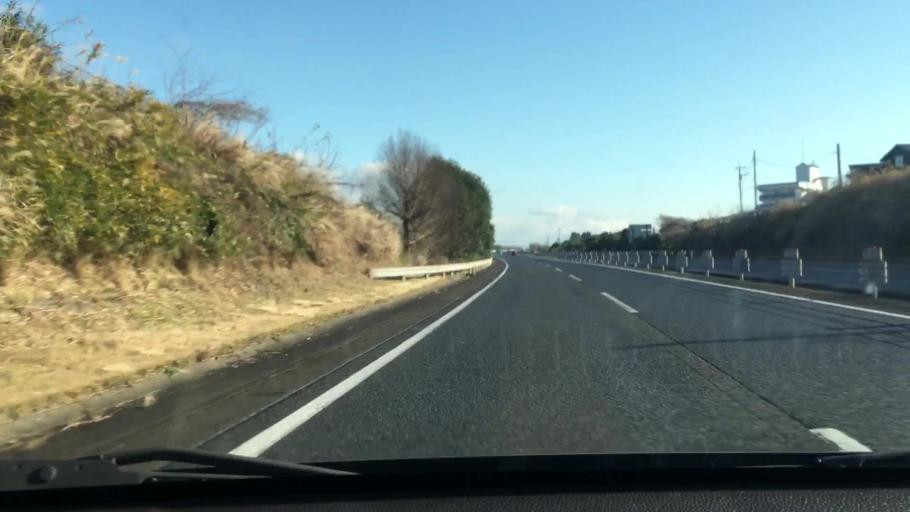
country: JP
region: Kagoshima
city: Kajiki
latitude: 31.8041
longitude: 130.7101
